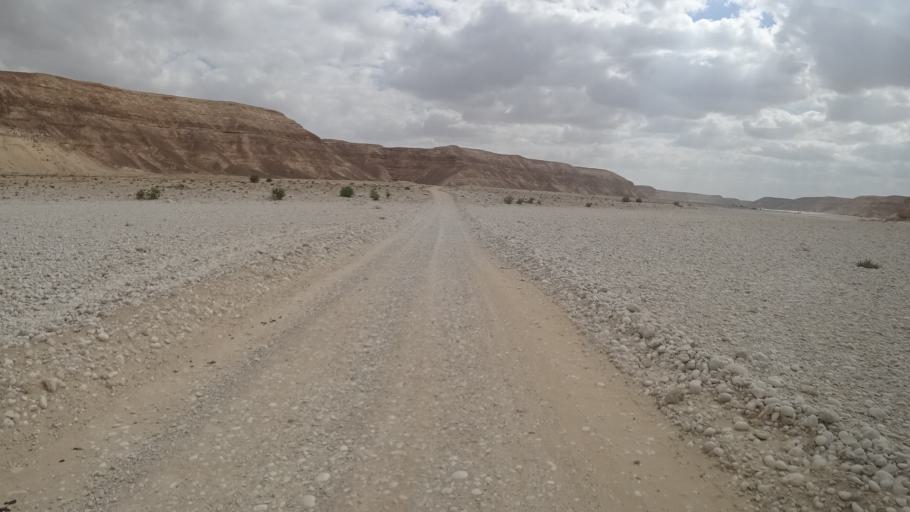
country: YE
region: Al Mahrah
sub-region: Shahan
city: Shihan as Sufla
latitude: 17.4647
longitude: 53.0067
